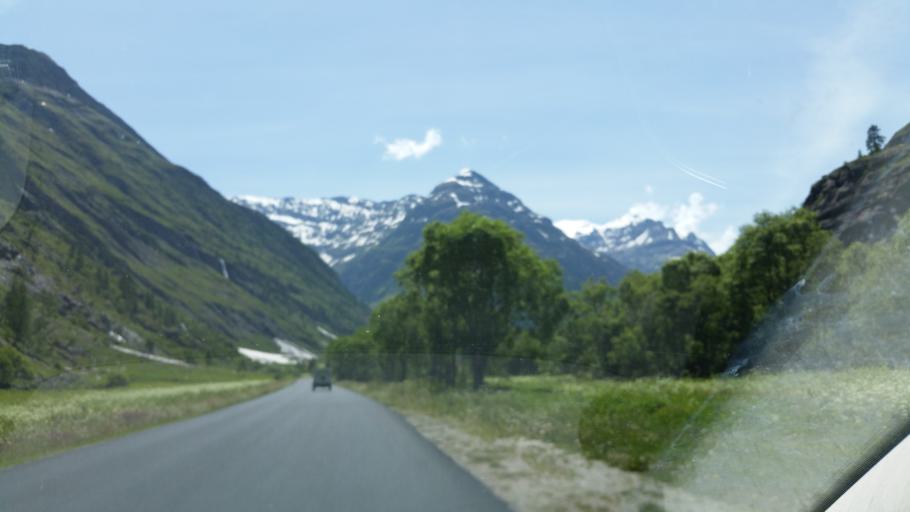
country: FR
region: Rhone-Alpes
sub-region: Departement de la Savoie
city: Val-d'Isere
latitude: 45.3491
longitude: 7.0299
